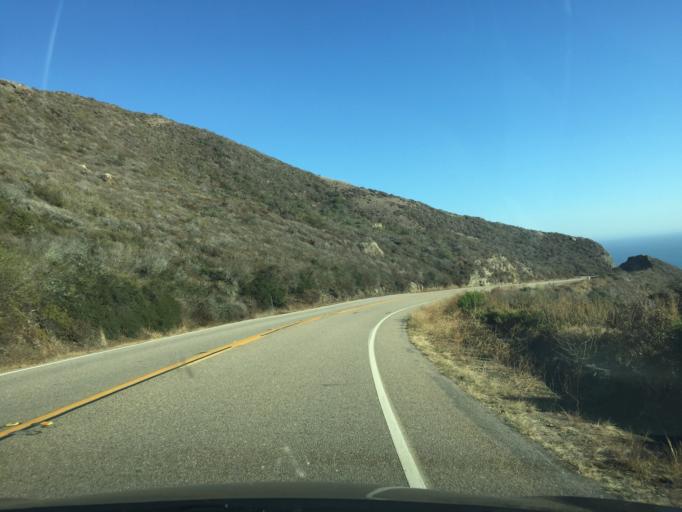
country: US
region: California
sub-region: San Luis Obispo County
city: Cambria
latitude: 35.8171
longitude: -121.3706
